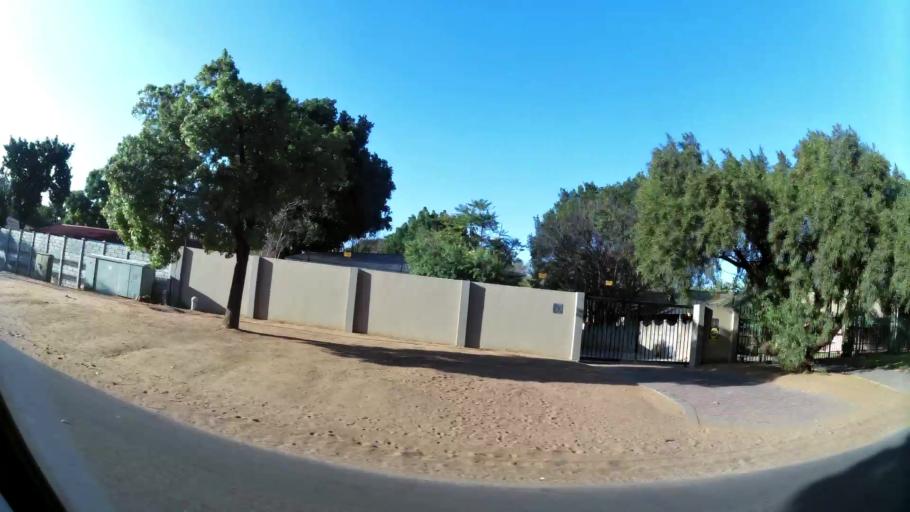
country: ZA
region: North-West
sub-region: Bojanala Platinum District Municipality
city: Rustenburg
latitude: -25.6768
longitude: 27.2334
